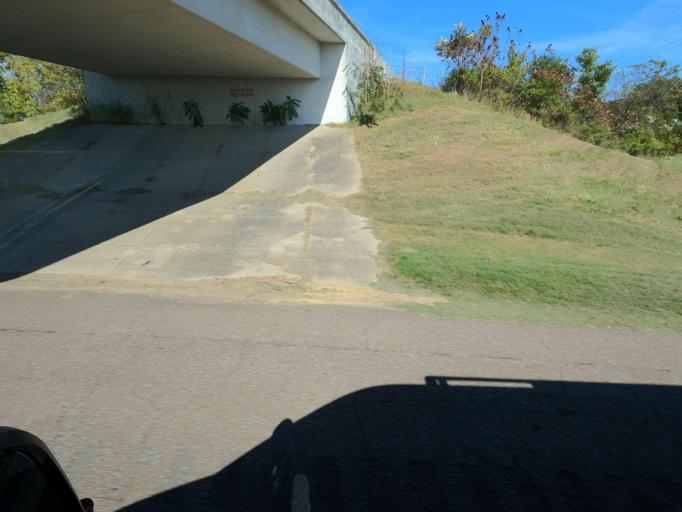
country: US
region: Tennessee
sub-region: Dyer County
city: Dyersburg
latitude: 36.0684
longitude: -89.3722
